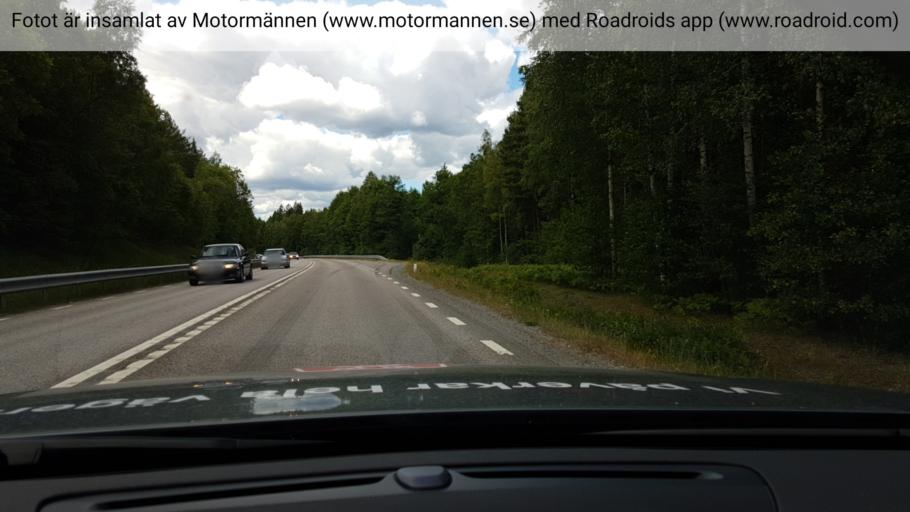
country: SE
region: Stockholm
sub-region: Osterakers Kommun
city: Akersberga
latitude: 59.4277
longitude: 18.2399
